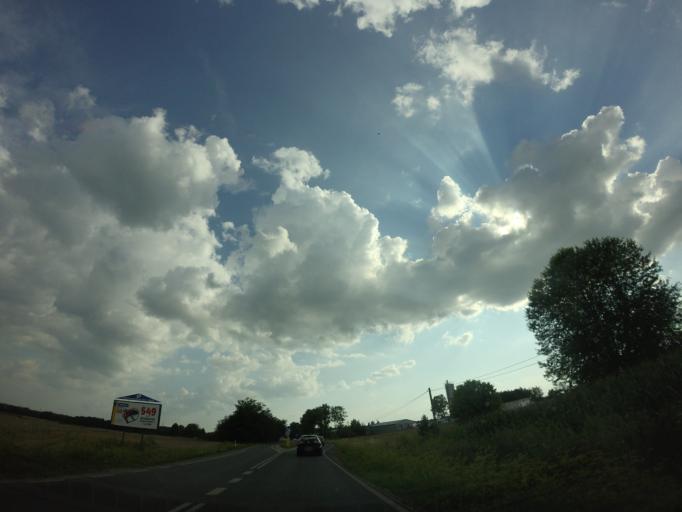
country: PL
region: Lublin Voivodeship
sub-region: Powiat lukowski
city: Lukow
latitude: 51.9081
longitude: 22.3679
